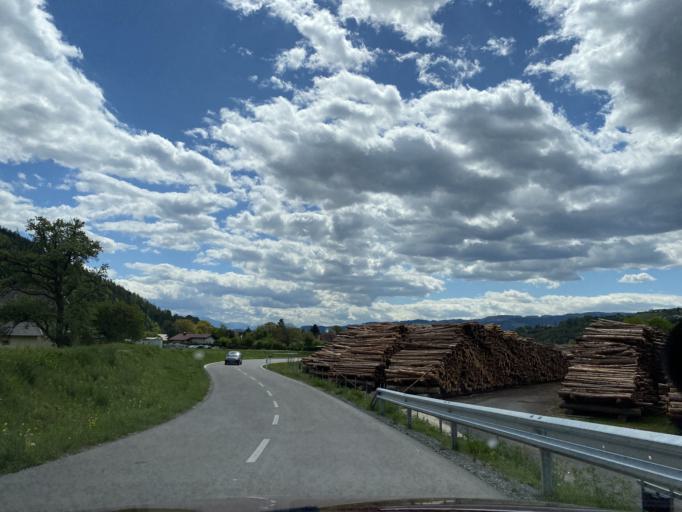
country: AT
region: Carinthia
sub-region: Politischer Bezirk Wolfsberg
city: Wolfsberg
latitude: 46.8587
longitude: 14.8516
